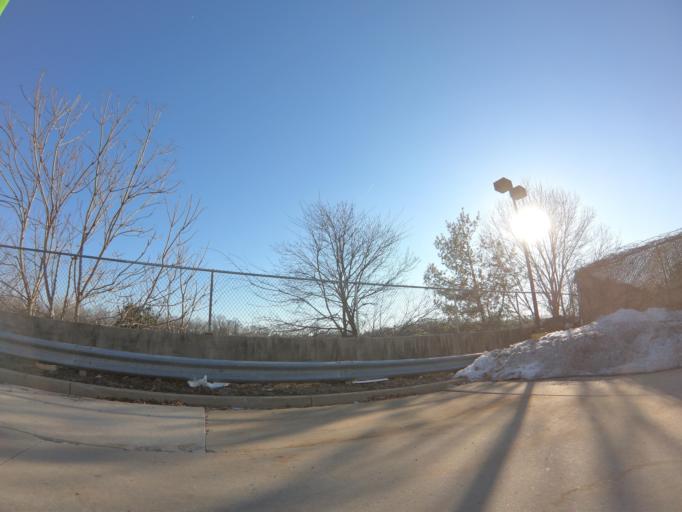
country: US
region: Maryland
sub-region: Frederick County
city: Frederick
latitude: 39.4454
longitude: -77.3877
